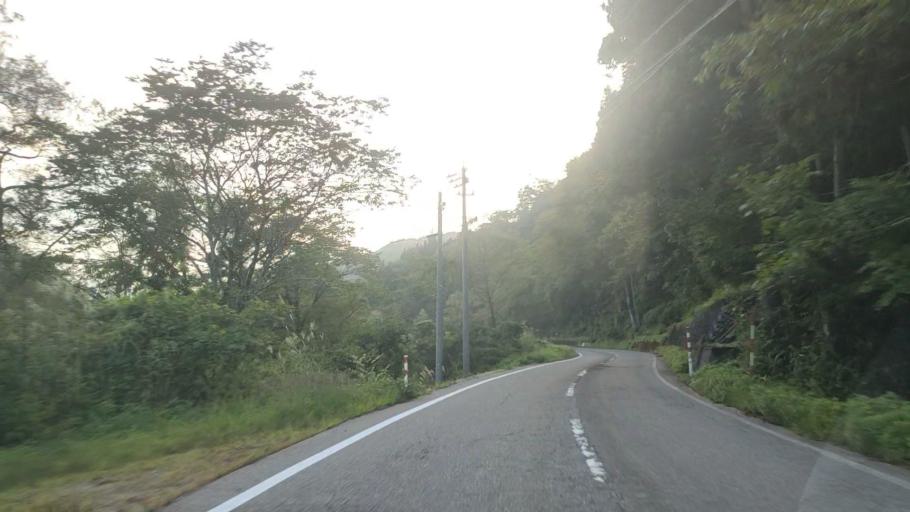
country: JP
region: Toyama
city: Yatsuomachi-higashikumisaka
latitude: 36.4627
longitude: 137.0448
